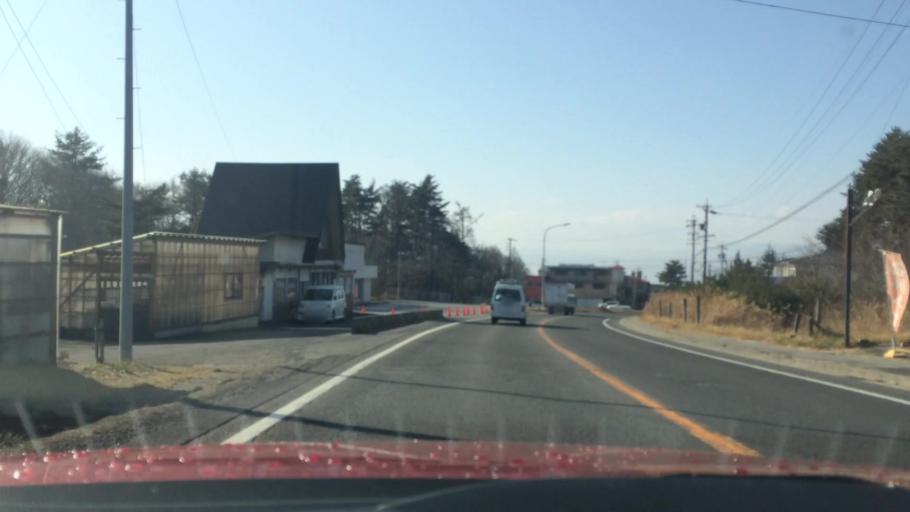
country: JP
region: Nagano
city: Komoro
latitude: 36.3293
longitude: 138.5170
